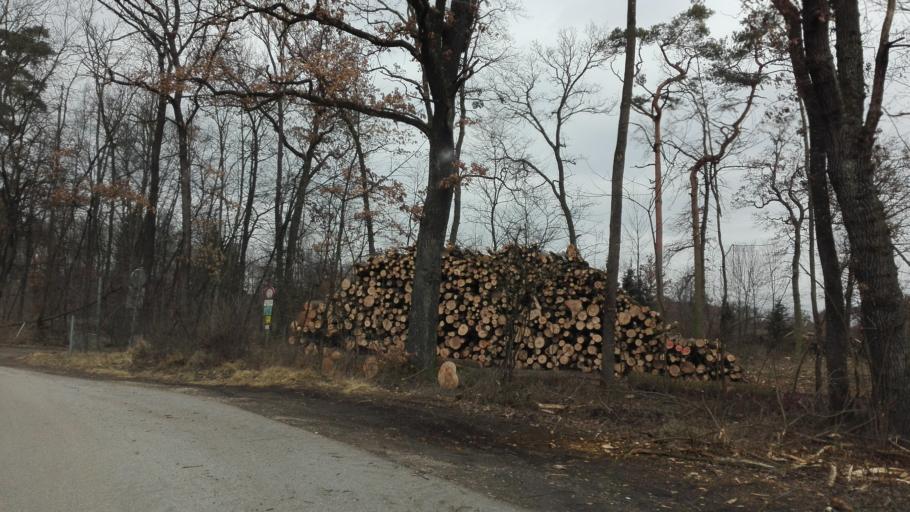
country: AT
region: Upper Austria
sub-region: Politischer Bezirk Linz-Land
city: Traun
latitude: 48.2352
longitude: 14.2177
